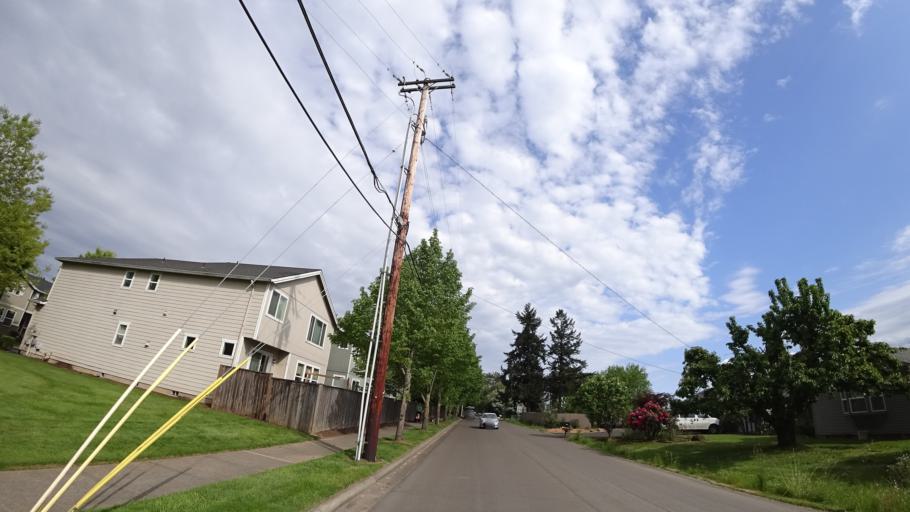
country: US
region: Oregon
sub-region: Washington County
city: Hillsboro
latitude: 45.4943
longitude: -122.9692
